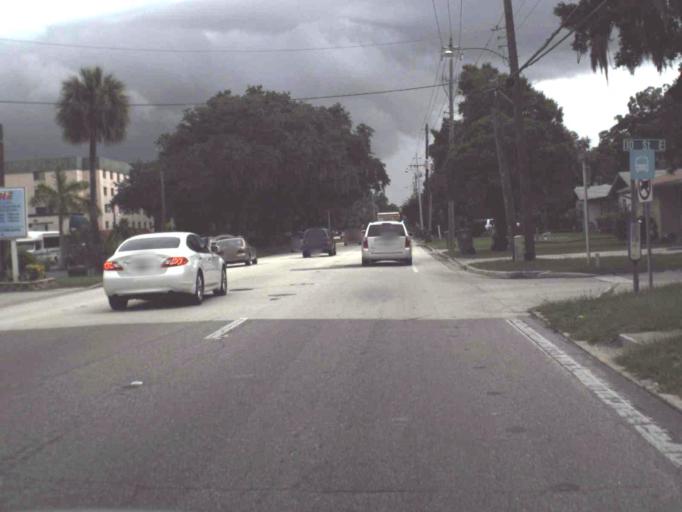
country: US
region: Florida
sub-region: Manatee County
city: Bradenton
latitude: 27.4940
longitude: -82.5537
